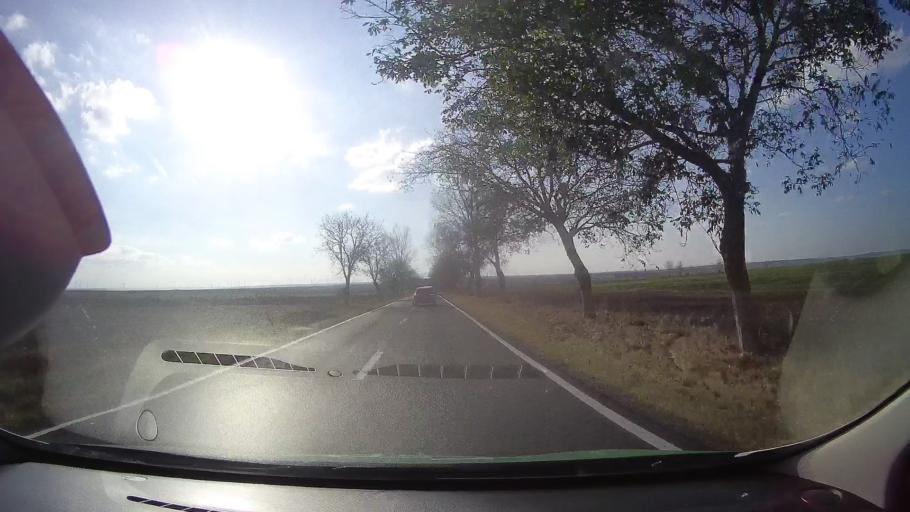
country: RO
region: Tulcea
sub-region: Comuna Topolog
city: Topolog
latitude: 44.8496
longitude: 28.3226
